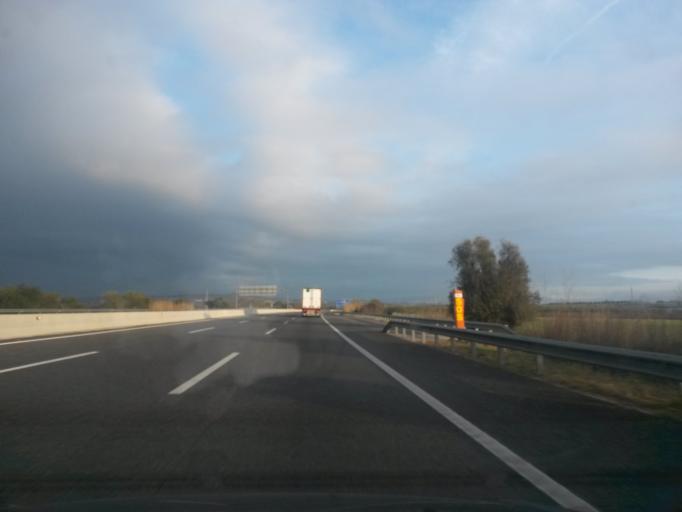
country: ES
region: Catalonia
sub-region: Provincia de Girona
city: Vilafant
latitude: 42.2331
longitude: 2.9369
